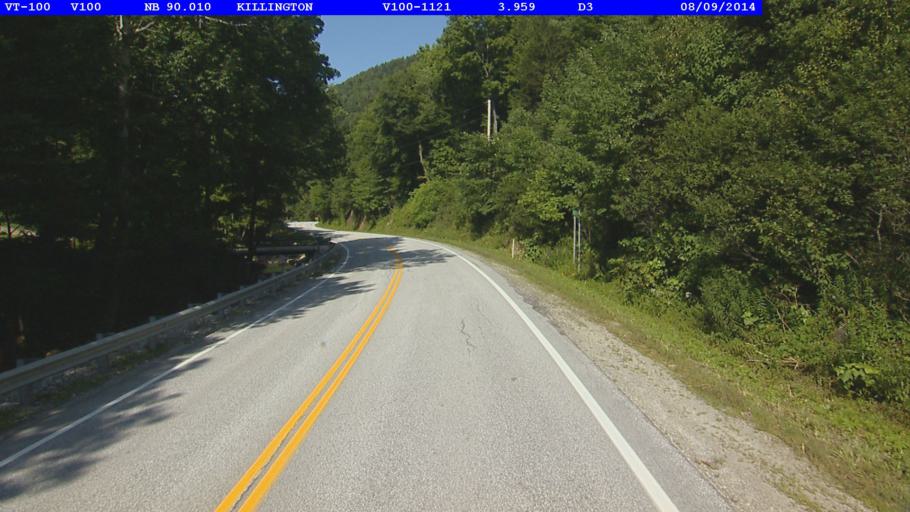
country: US
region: Vermont
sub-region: Rutland County
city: Rutland
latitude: 43.7177
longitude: -72.8248
